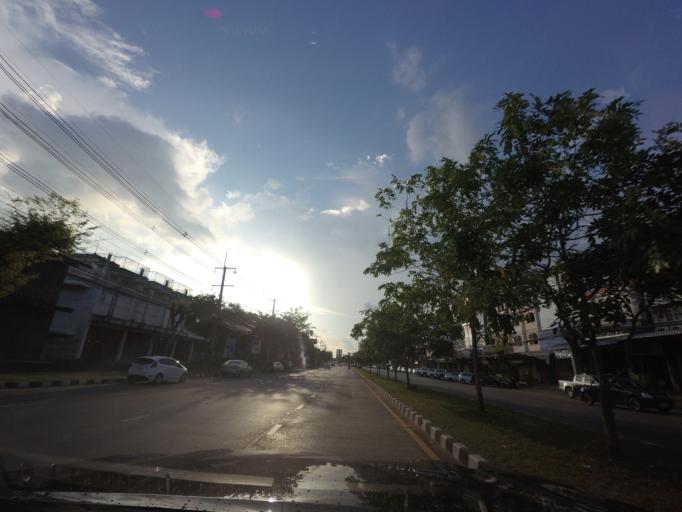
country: TH
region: Khon Kaen
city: Khon Kaen
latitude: 16.4285
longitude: 102.8557
